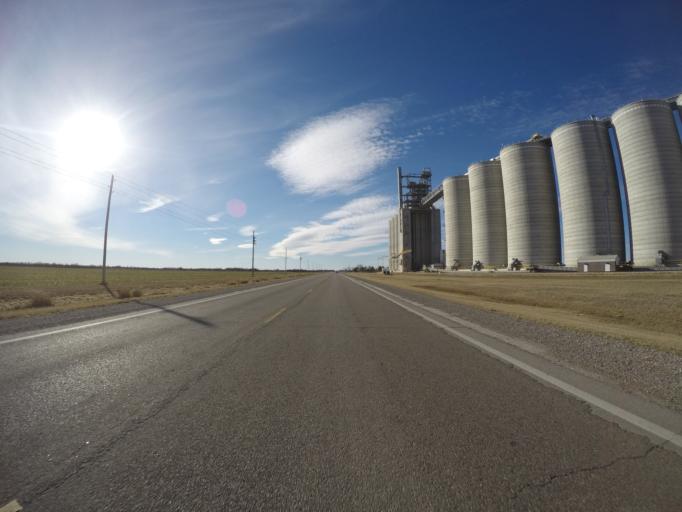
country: US
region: Kansas
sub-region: McPherson County
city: Moundridge
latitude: 38.3769
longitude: -97.4679
